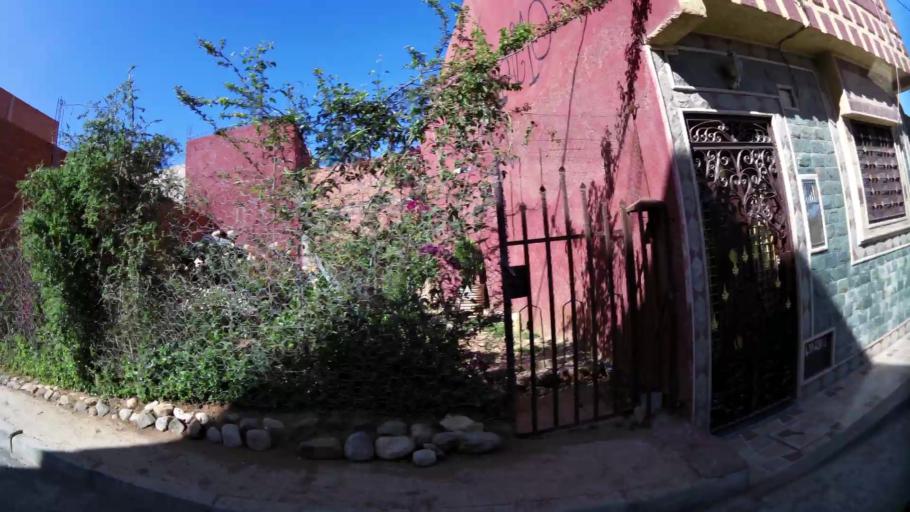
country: MA
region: Oriental
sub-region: Oujda-Angad
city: Oujda
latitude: 34.6445
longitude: -1.9506
